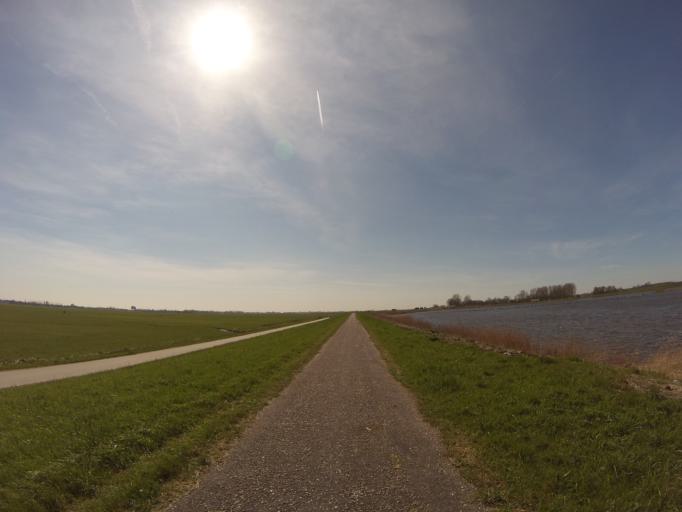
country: NL
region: Gelderland
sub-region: Gemeente Nijkerk
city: Nijkerk
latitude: 52.2594
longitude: 5.4826
